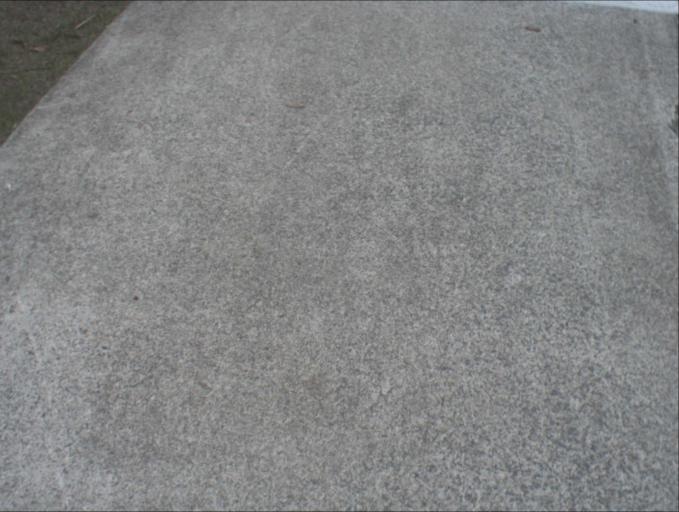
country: AU
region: Queensland
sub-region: Logan
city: Logan Reserve
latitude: -27.6838
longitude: 153.0811
